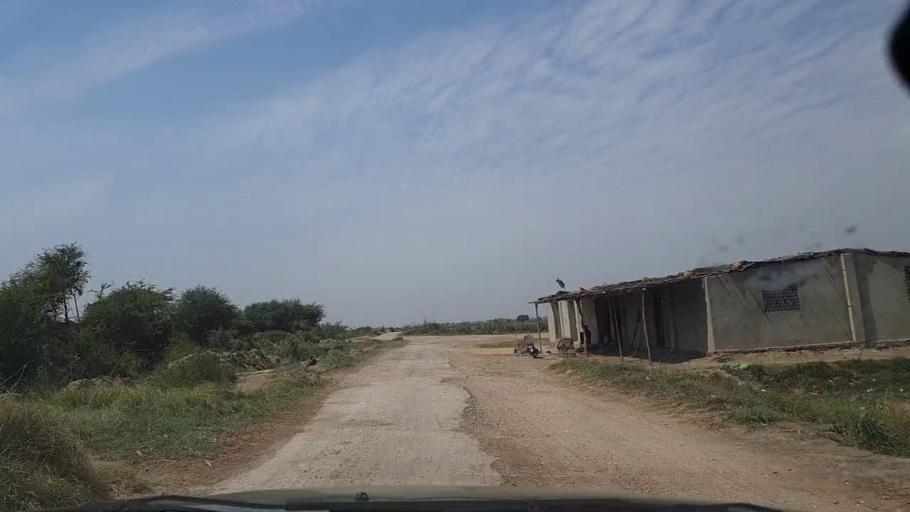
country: PK
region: Sindh
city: Mirpur Batoro
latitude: 24.6427
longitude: 68.1447
